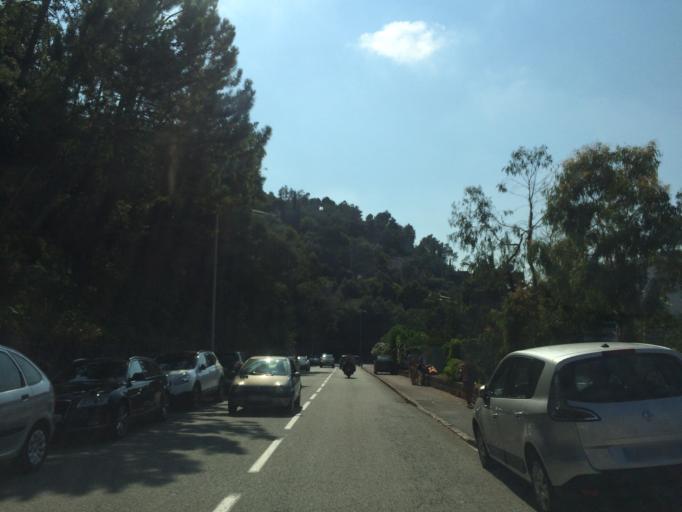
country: FR
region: Provence-Alpes-Cote d'Azur
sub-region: Departement des Alpes-Maritimes
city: Theoule-sur-Mer
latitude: 43.5053
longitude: 6.9477
